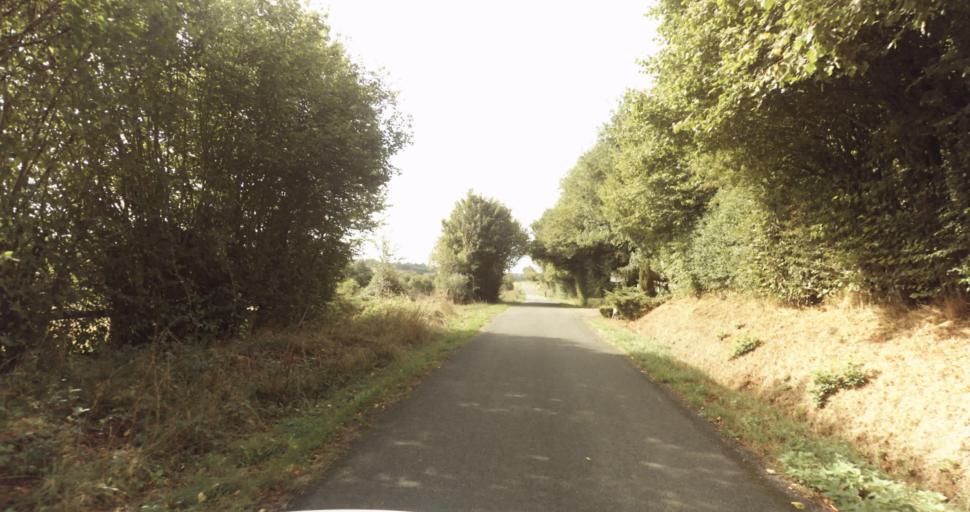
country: FR
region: Lower Normandy
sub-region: Departement de l'Orne
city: Gace
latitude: 48.8454
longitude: 0.3886
